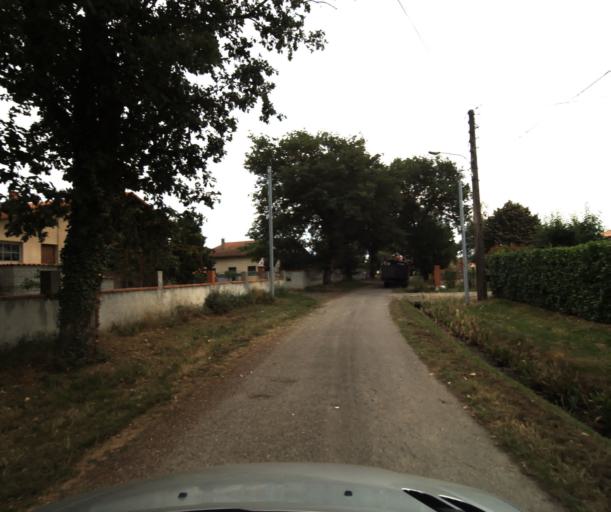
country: FR
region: Midi-Pyrenees
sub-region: Departement de la Haute-Garonne
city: Lacasse
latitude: 43.4224
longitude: 1.2706
